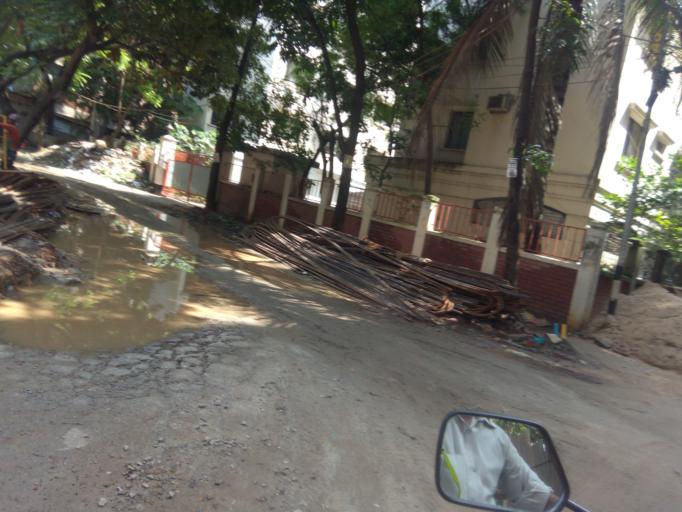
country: BD
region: Dhaka
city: Azimpur
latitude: 23.7590
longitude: 90.3716
